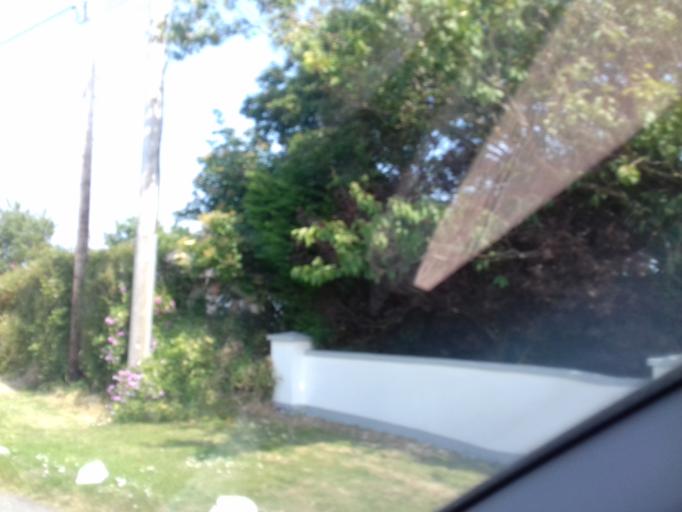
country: IE
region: Leinster
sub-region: An Mhi
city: Stamullin
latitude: 53.5969
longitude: -6.3168
